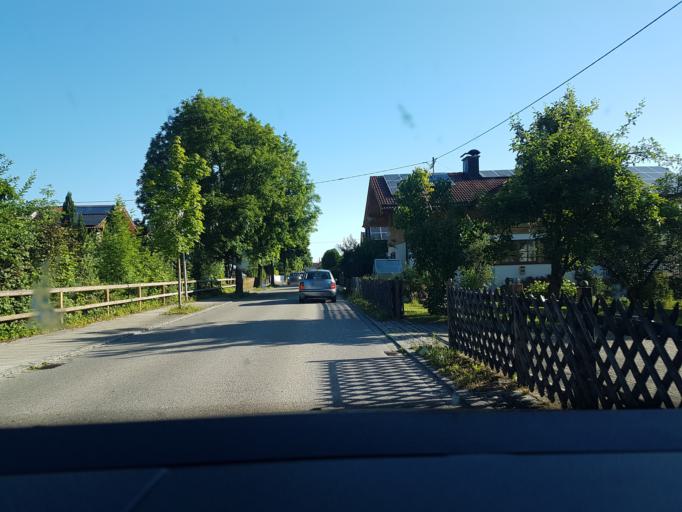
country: DE
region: Bavaria
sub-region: Upper Bavaria
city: Ainring
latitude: 47.8288
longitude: 12.9533
